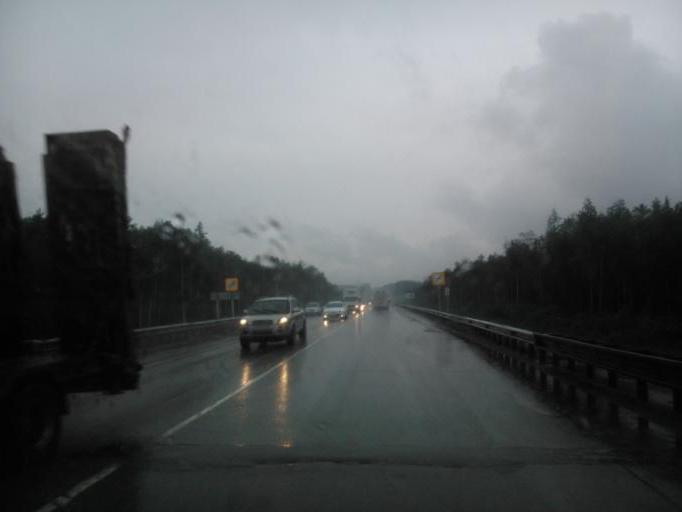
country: RU
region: Sverdlovsk
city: Severka
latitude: 56.8824
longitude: 60.3858
